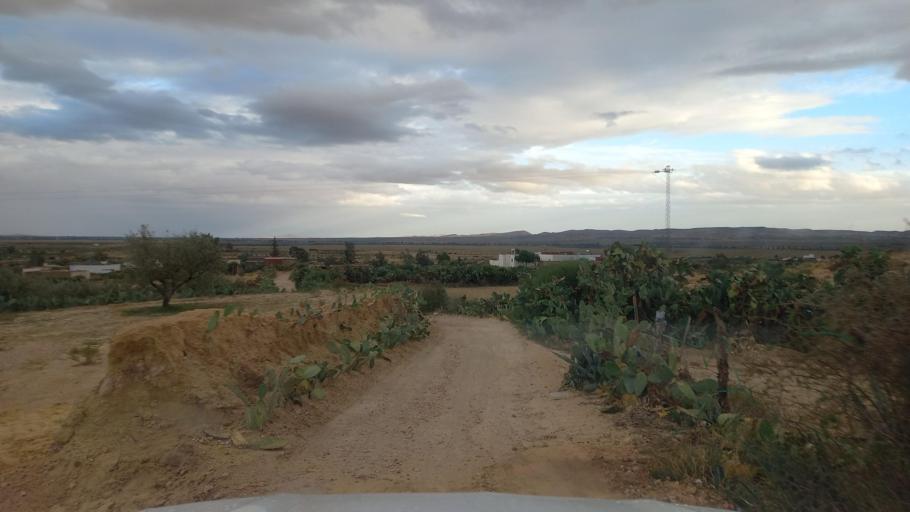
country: TN
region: Al Qasrayn
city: Kasserine
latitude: 35.2582
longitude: 8.9350
